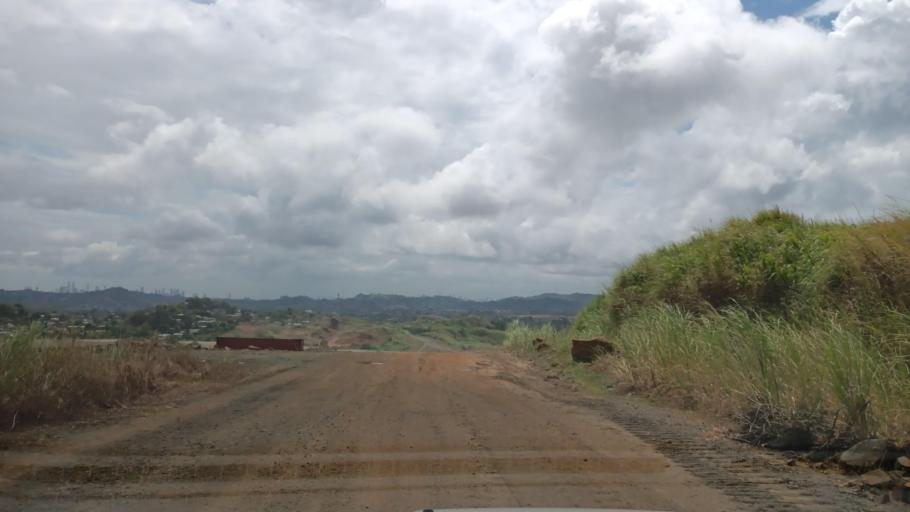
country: PA
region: Panama
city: Las Cumbres
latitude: 9.1113
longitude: -79.4985
